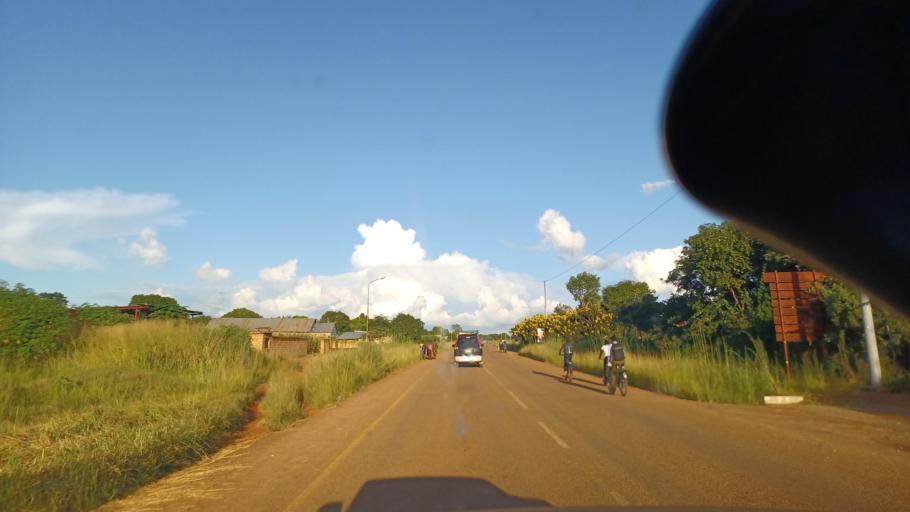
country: ZM
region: North-Western
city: Kalengwa
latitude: -13.1375
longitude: 25.0101
